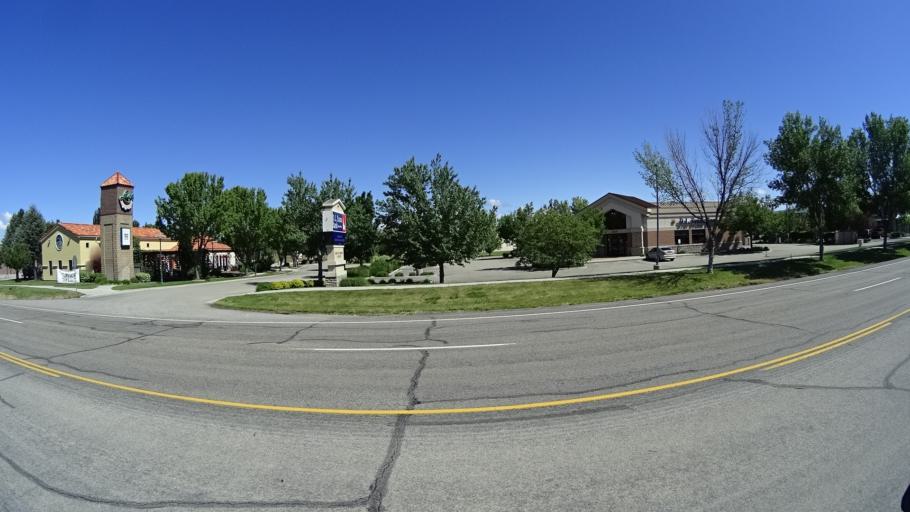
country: US
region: Idaho
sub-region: Ada County
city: Meridian
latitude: 43.6194
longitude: -116.3629
